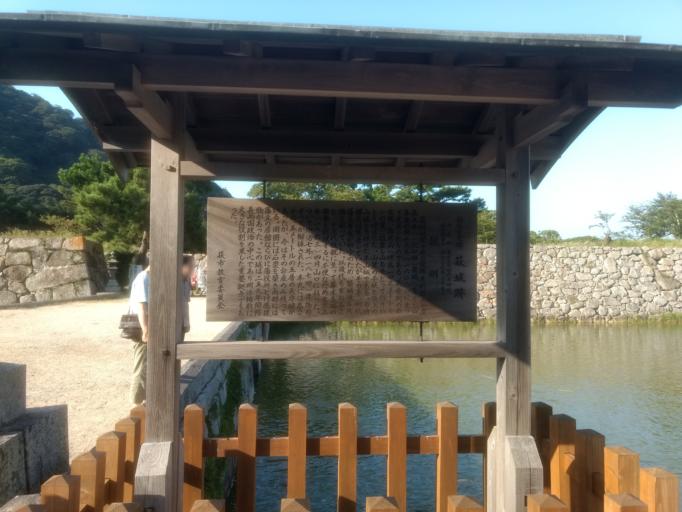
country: JP
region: Yamaguchi
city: Hagi
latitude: 34.4169
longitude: 131.3838
